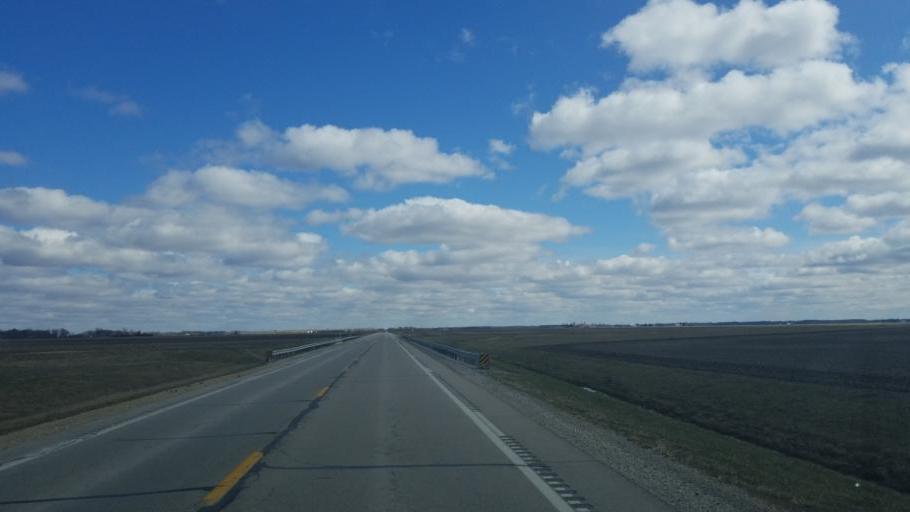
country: US
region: Illinois
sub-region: Douglas County
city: Villa Grove
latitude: 39.7920
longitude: -88.0990
